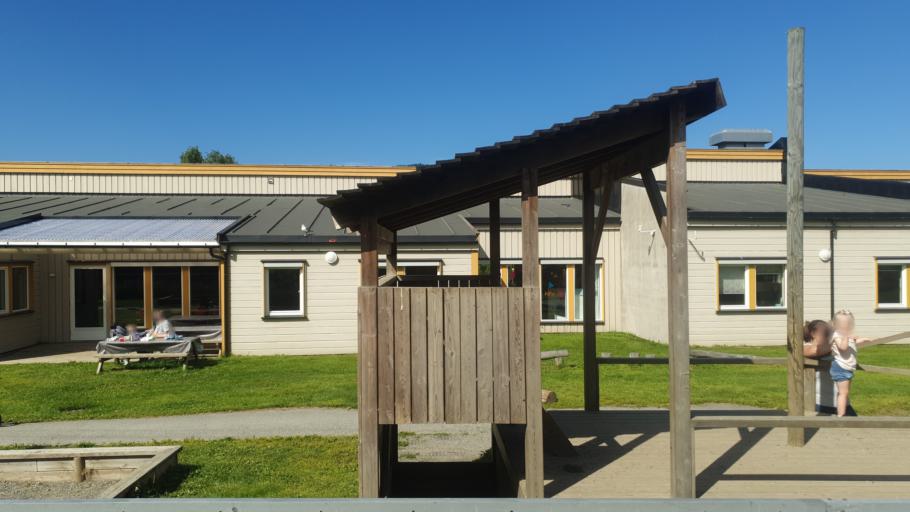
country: NO
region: Sor-Trondelag
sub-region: Orkdal
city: Orkanger
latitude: 63.2862
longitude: 9.8416
